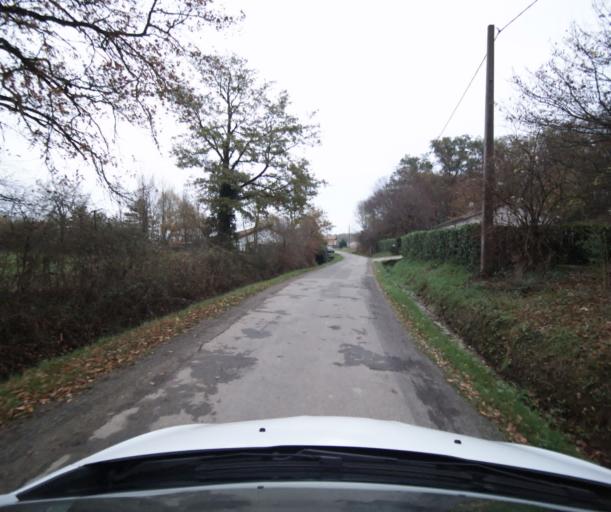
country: FR
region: Midi-Pyrenees
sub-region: Departement du Tarn-et-Garonne
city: Moissac
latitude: 44.0798
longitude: 1.1440
